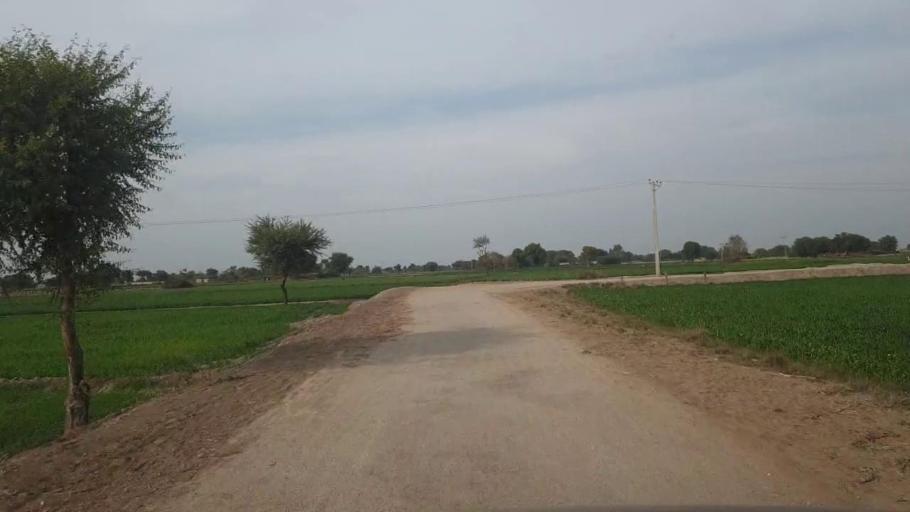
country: PK
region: Sindh
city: Shahpur Chakar
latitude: 26.1105
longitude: 68.5192
